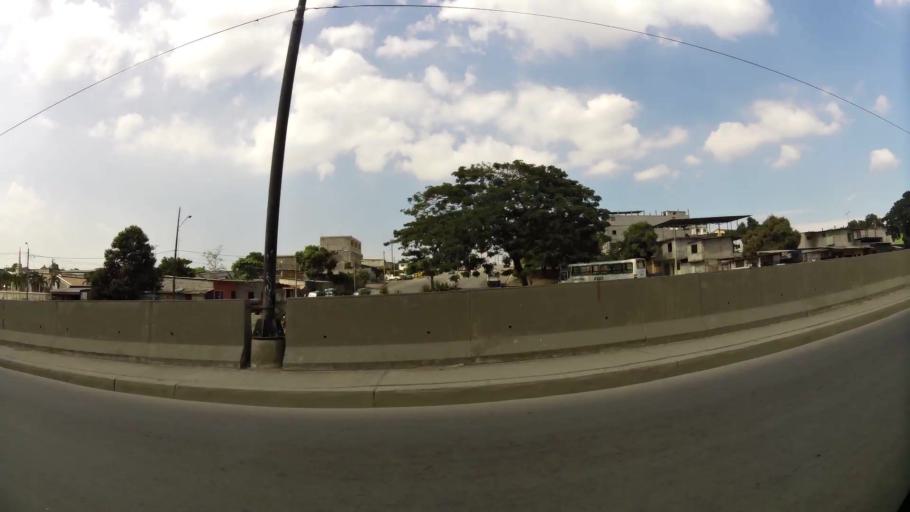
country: EC
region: Guayas
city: Santa Lucia
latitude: -2.1297
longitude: -79.9489
